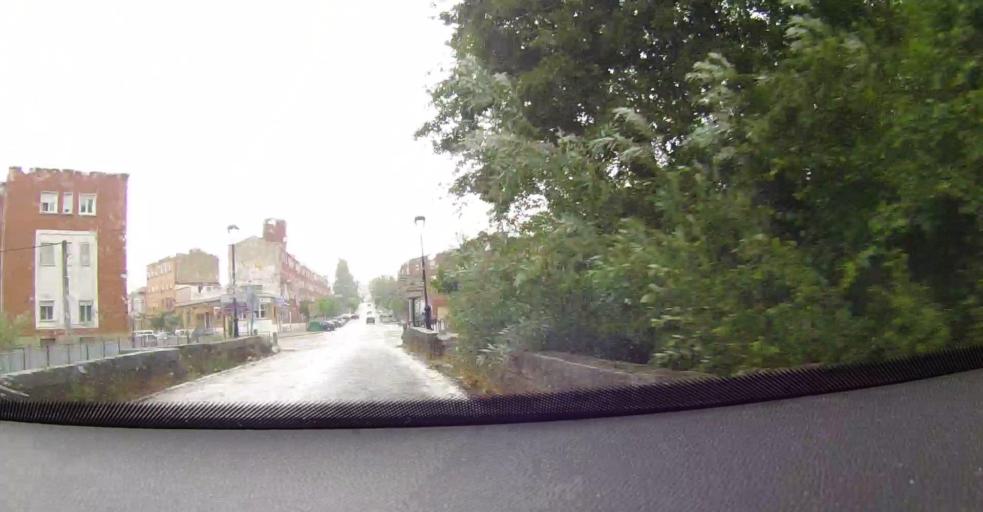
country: ES
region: Castille and Leon
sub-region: Provincia de Palencia
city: Saldana
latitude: 42.5178
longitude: -4.7367
